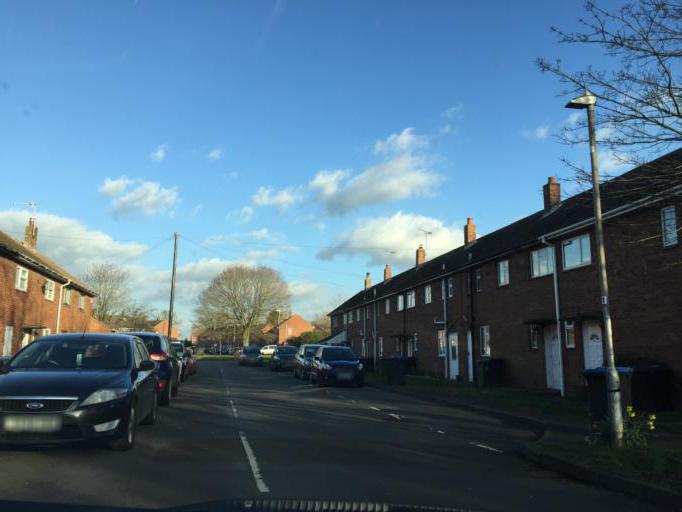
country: GB
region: England
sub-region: Warwickshire
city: Harbury
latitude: 52.1990
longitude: -1.4876
